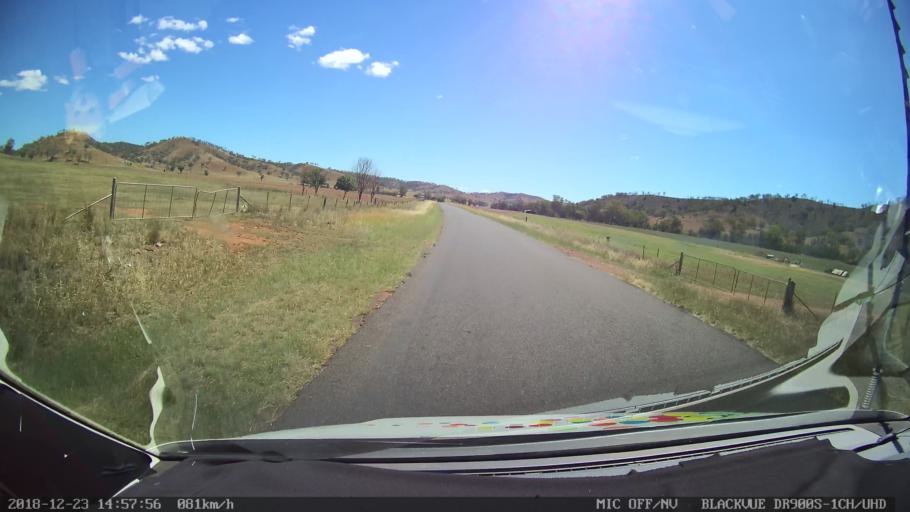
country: AU
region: New South Wales
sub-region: Tamworth Municipality
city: Manilla
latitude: -30.7123
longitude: 150.8185
